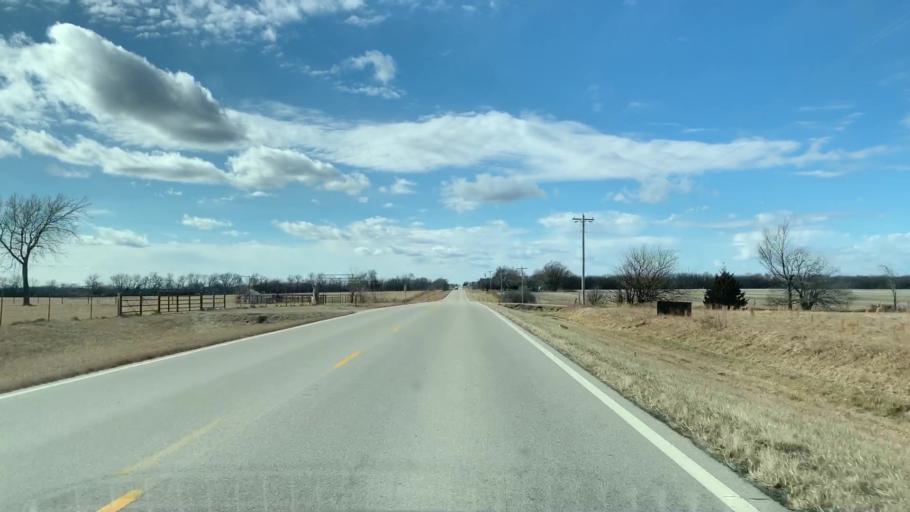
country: US
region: Kansas
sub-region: Neosho County
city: Chanute
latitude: 37.5291
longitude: -95.4149
